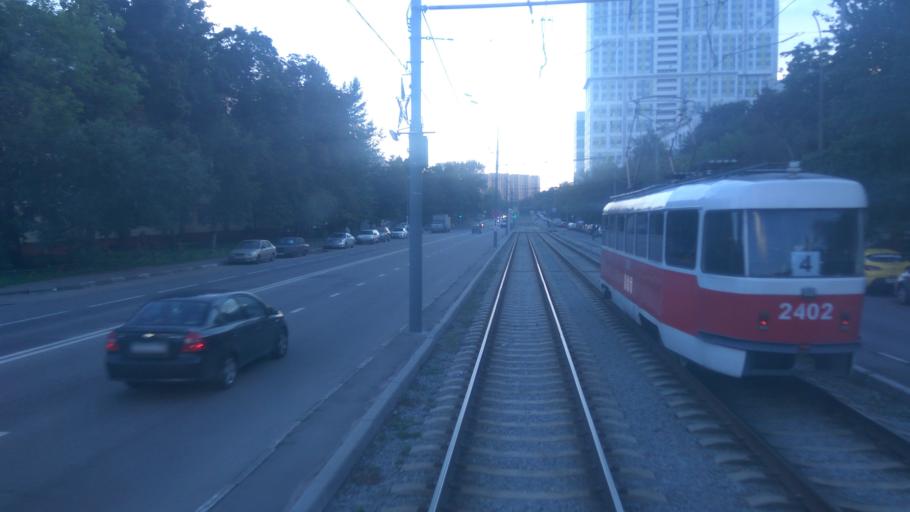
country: RU
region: Moskovskaya
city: Bogorodskoye
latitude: 55.8117
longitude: 37.7328
